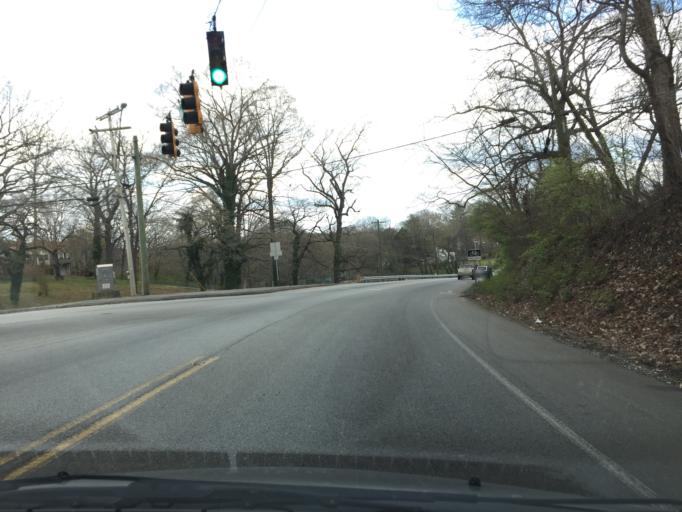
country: US
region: Tennessee
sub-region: Hamilton County
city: East Chattanooga
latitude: 35.0795
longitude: -85.2274
